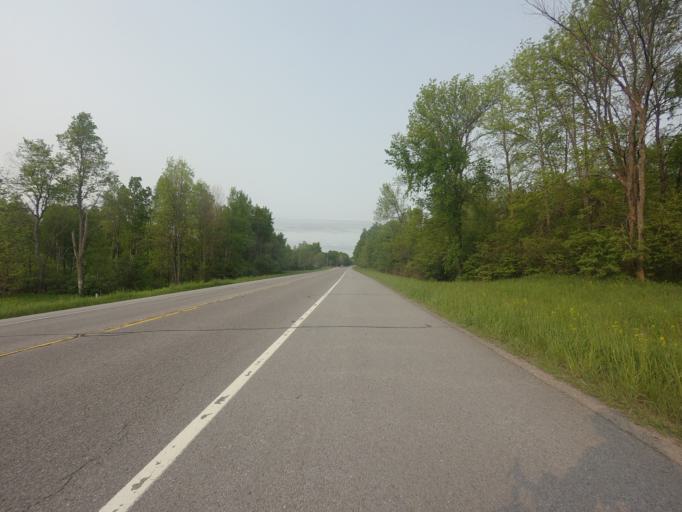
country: US
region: New York
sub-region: Jefferson County
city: Carthage
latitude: 44.0582
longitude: -75.5438
